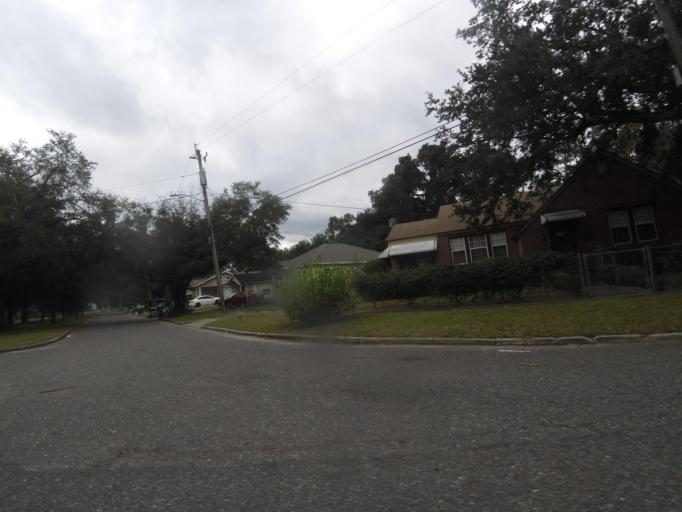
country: US
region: Florida
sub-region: Duval County
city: Jacksonville
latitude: 30.3796
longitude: -81.6542
